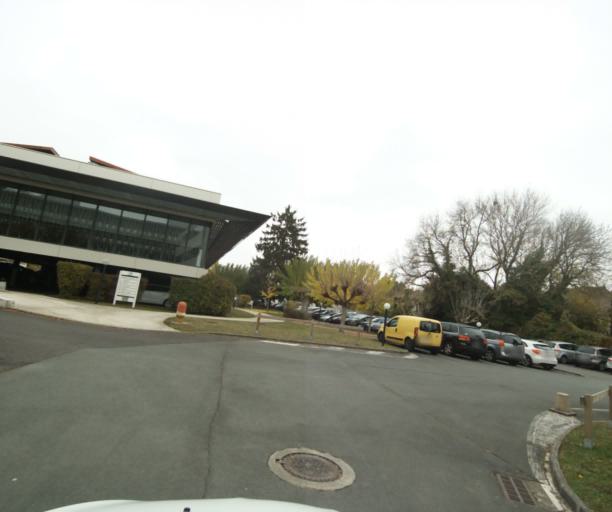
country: FR
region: Poitou-Charentes
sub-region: Departement de la Charente-Maritime
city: Saintes
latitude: 45.7475
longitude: -0.6262
